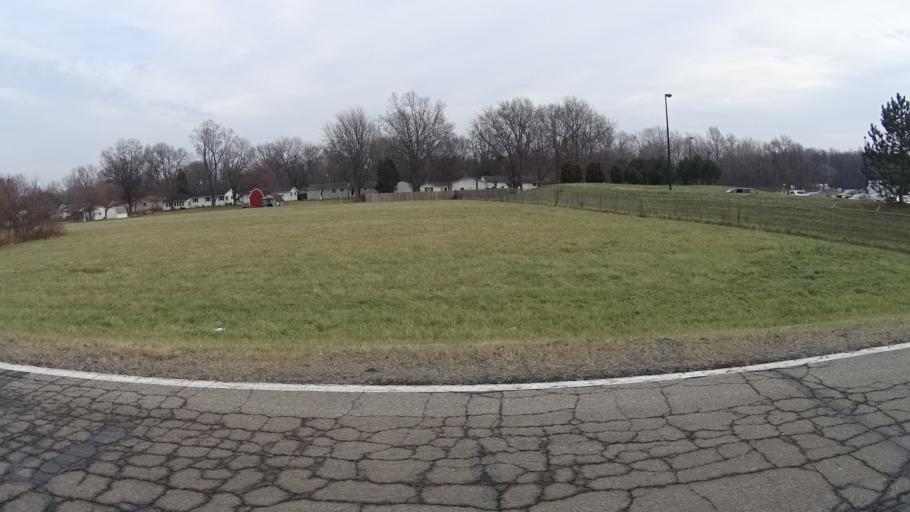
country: US
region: Ohio
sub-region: Lorain County
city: Amherst
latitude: 41.3813
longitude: -82.2235
